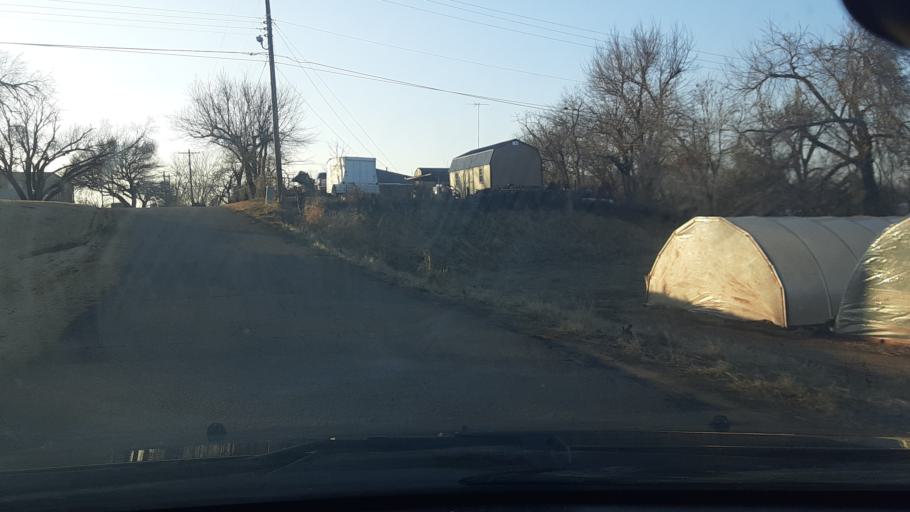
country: US
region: Oklahoma
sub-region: Logan County
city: Guthrie
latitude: 35.8874
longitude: -97.4217
